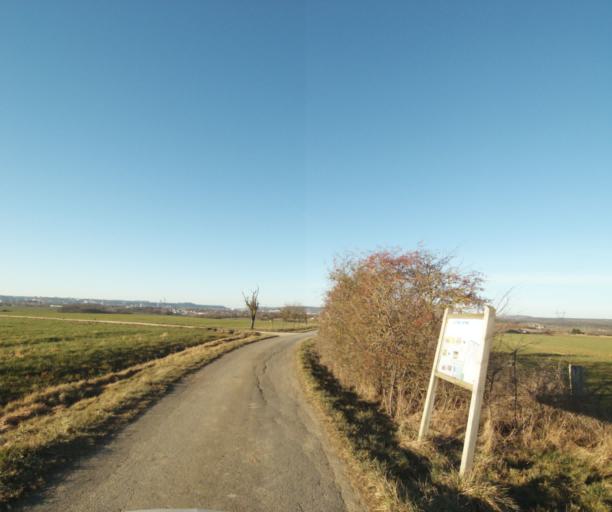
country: FR
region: Lorraine
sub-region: Departement de Meurthe-et-Moselle
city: Laneuveville-devant-Nancy
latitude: 48.6371
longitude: 6.2315
